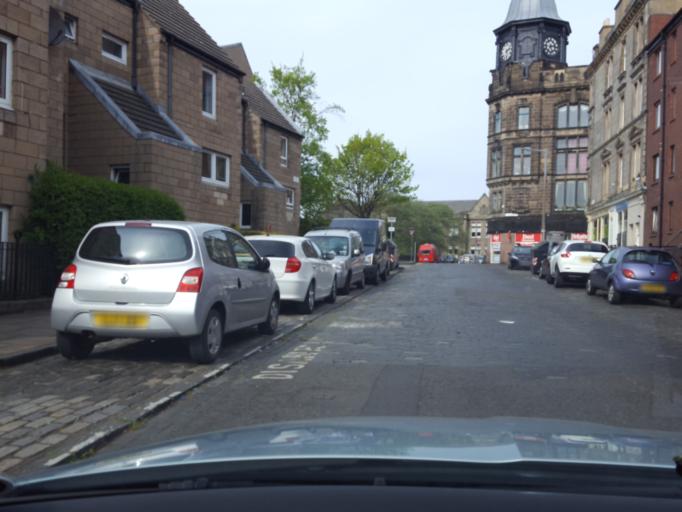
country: GB
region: Scotland
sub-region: West Lothian
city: Seafield
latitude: 55.9733
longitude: -3.1776
